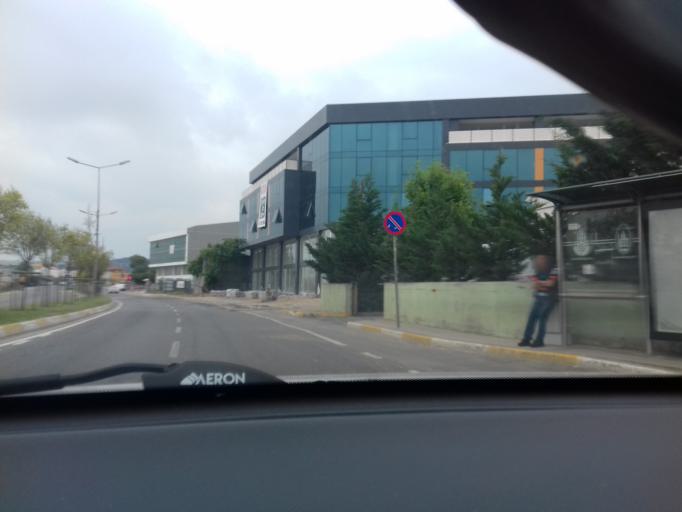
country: TR
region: Istanbul
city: Icmeler
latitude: 40.8941
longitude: 29.3548
